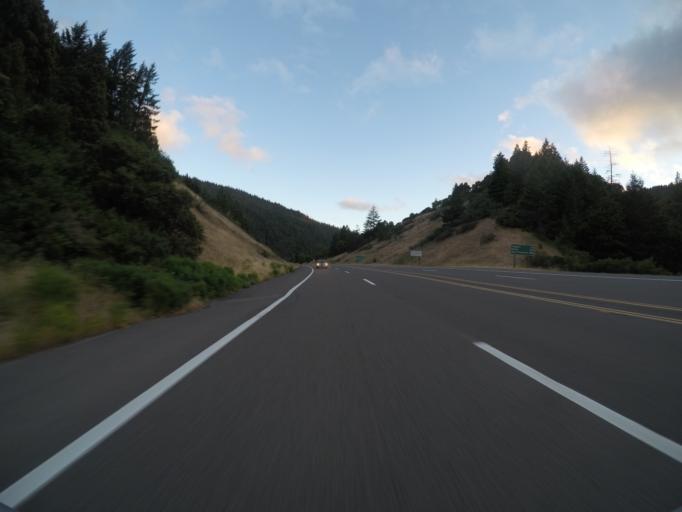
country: US
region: California
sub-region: Humboldt County
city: Redway
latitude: 39.9967
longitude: -123.7880
